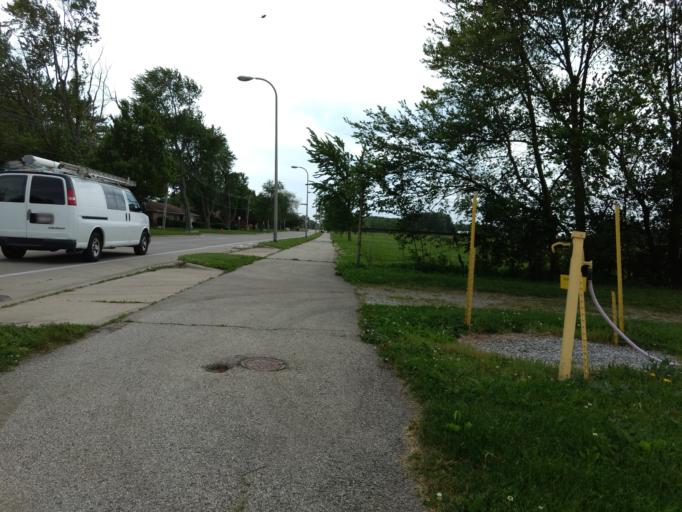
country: US
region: Illinois
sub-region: Champaign County
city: Urbana
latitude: 40.0876
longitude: -88.2096
